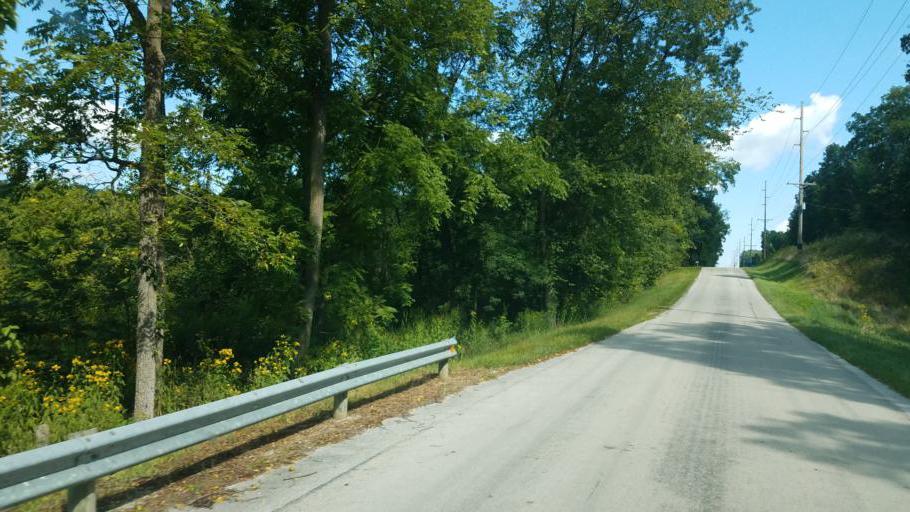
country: US
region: Ohio
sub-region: Wyandot County
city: Carey
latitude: 40.9532
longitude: -83.3194
